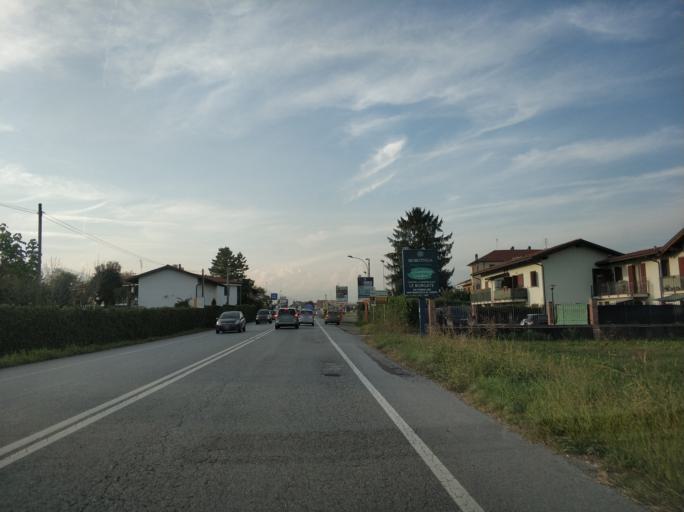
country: IT
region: Piedmont
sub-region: Provincia di Torino
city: Caselle Torinese
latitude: 45.1931
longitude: 7.6294
